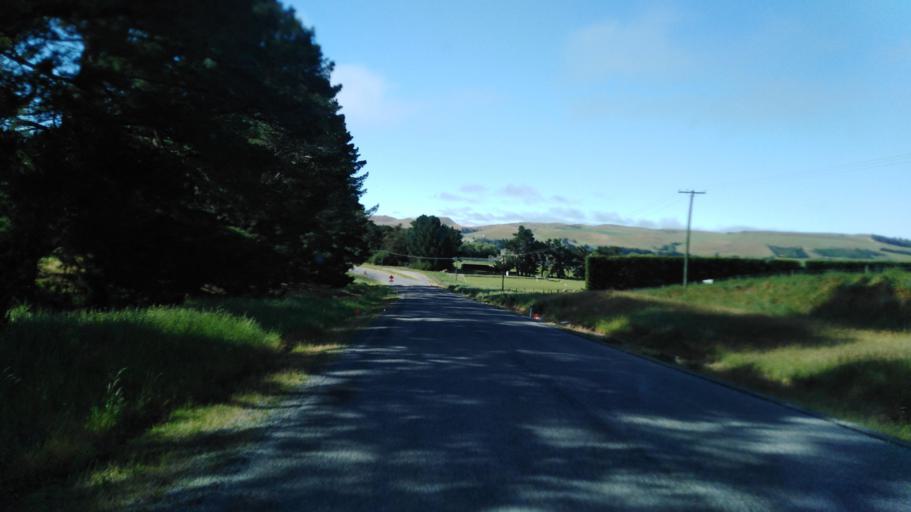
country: NZ
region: Canterbury
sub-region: Hurunui District
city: Amberley
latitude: -42.9491
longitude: 172.7076
